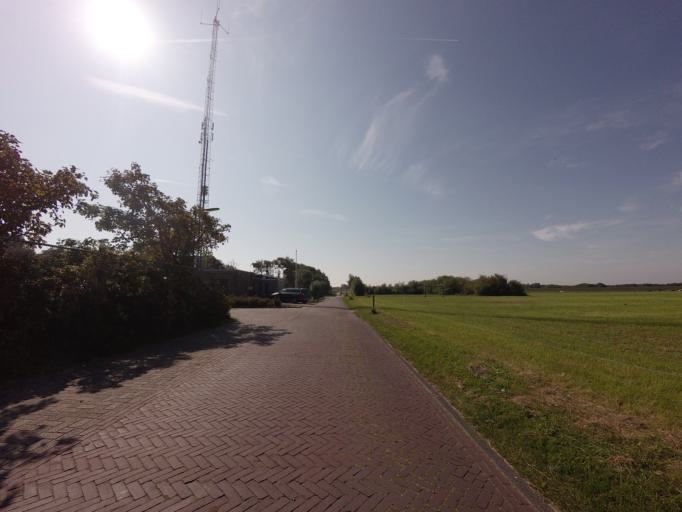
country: NL
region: Friesland
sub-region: Gemeente Schiermonnikoog
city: Schiermonnikoog
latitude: 53.4767
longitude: 6.1546
